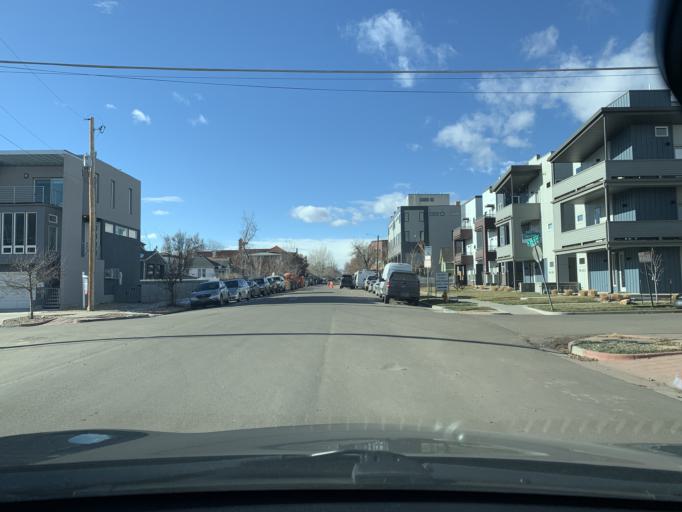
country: US
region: Colorado
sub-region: Denver County
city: Denver
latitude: 39.7536
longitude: -105.0219
